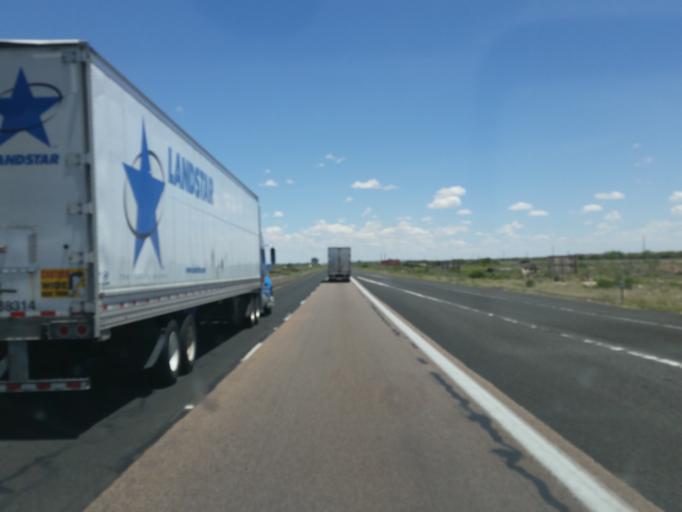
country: US
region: Arizona
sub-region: Navajo County
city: Joseph City
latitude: 34.9685
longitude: -110.4297
